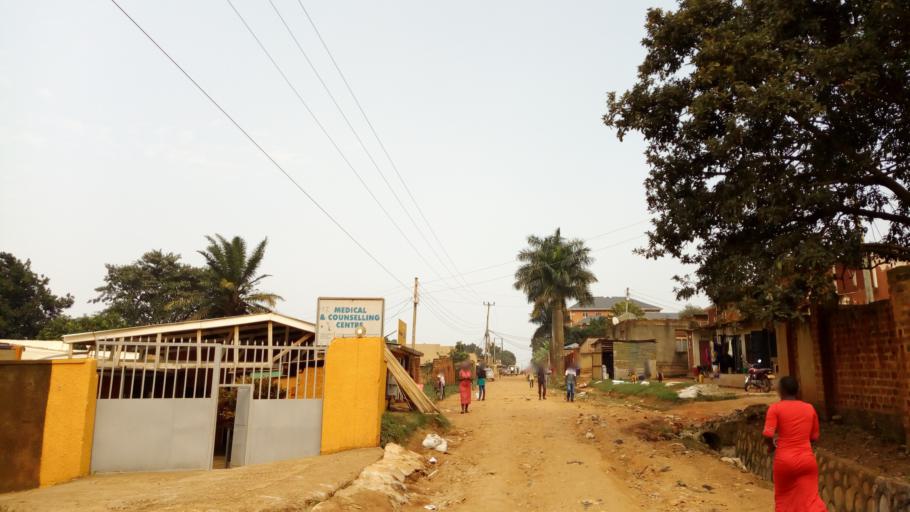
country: UG
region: Central Region
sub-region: Wakiso District
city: Kireka
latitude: 0.3188
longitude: 32.6466
